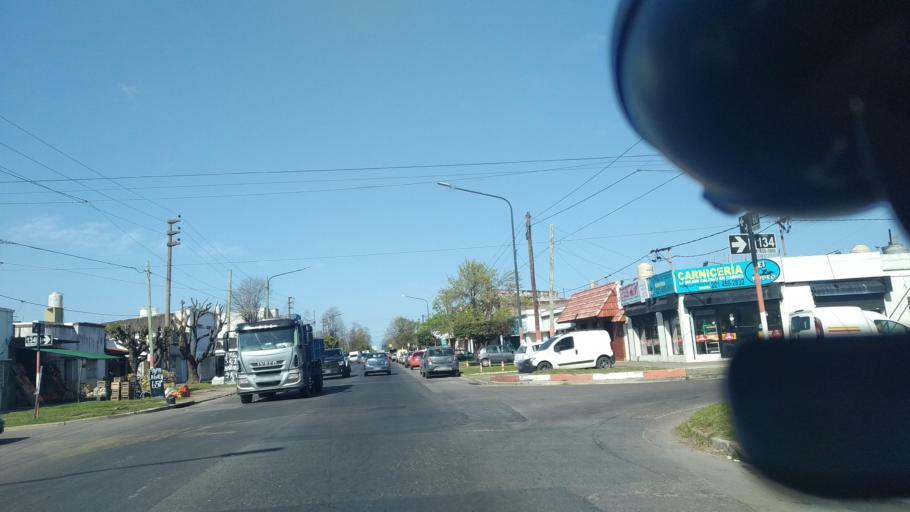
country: AR
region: Buenos Aires
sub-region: Partido de La Plata
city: La Plata
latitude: -34.9516
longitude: -57.9629
